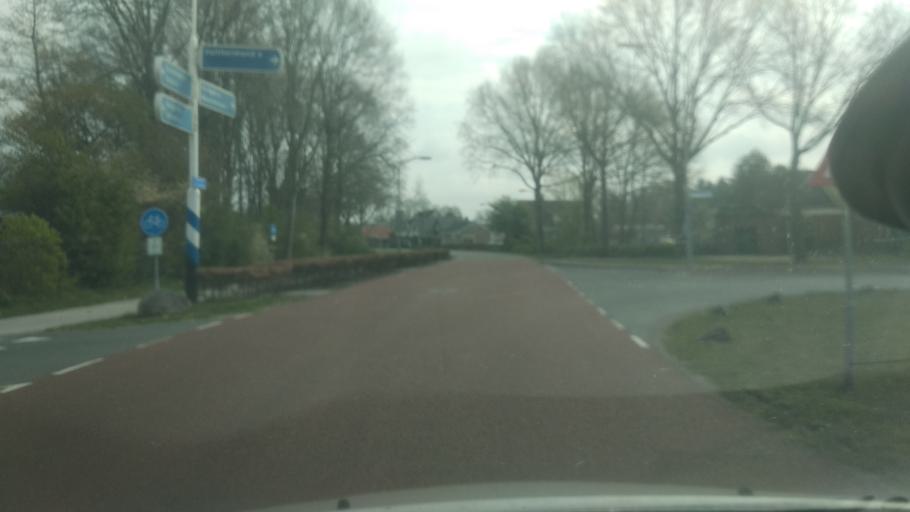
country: NL
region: Groningen
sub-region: Gemeente Stadskanaal
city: Stadskanaal
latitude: 52.9030
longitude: 6.9148
